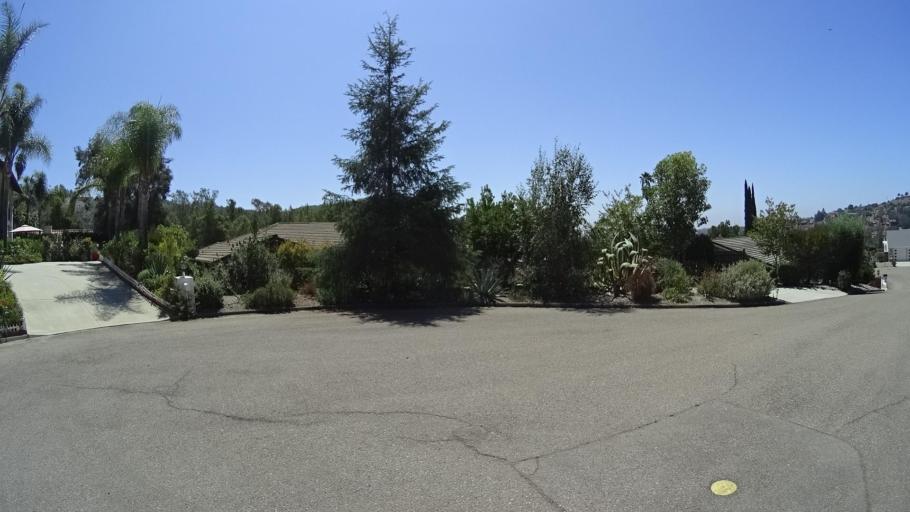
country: US
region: California
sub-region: San Diego County
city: Bonsall
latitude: 33.3384
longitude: -117.1827
